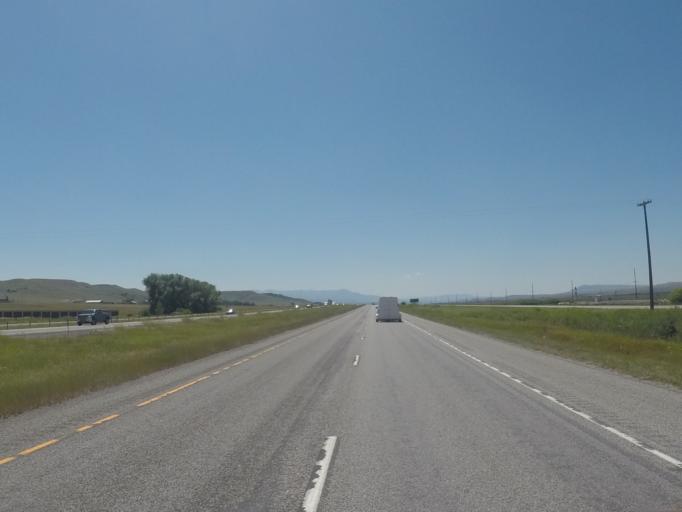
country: US
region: Montana
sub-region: Sweet Grass County
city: Big Timber
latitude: 45.8200
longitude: -109.9879
